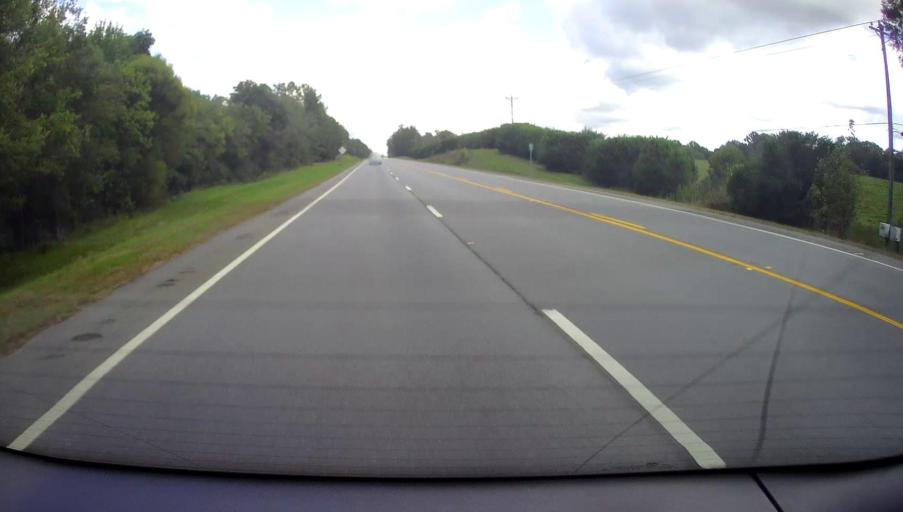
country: US
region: Georgia
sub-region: Baldwin County
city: Milledgeville
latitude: 33.0675
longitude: -83.3541
